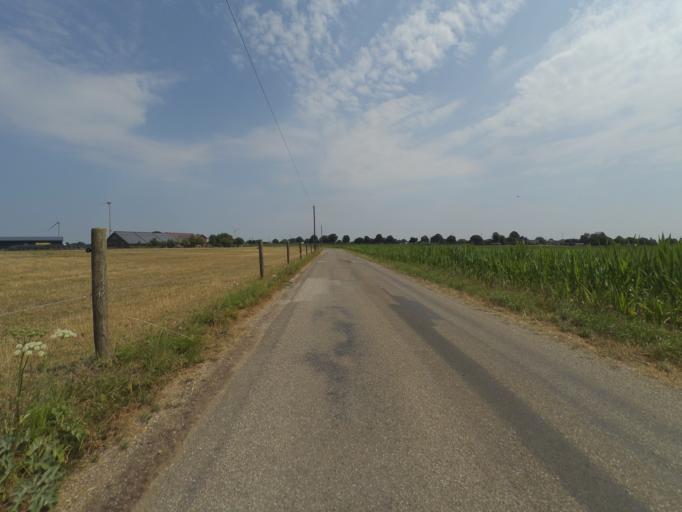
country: DE
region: North Rhine-Westphalia
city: Rees
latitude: 51.7836
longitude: 6.4411
